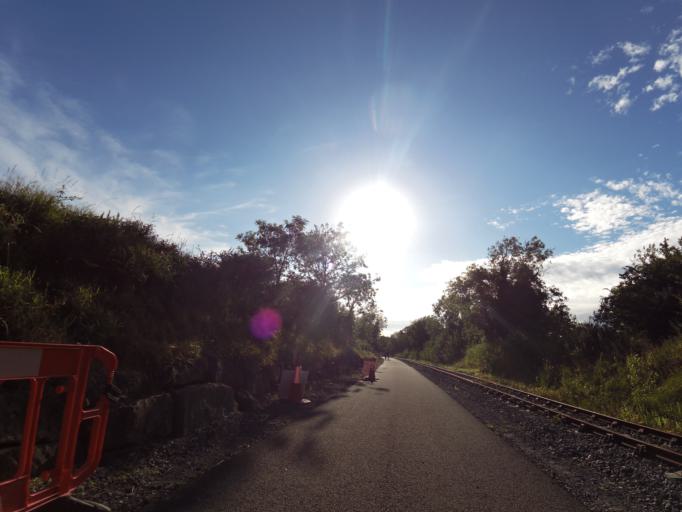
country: IE
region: Munster
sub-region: Waterford
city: Waterford
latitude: 52.2735
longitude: -7.1506
